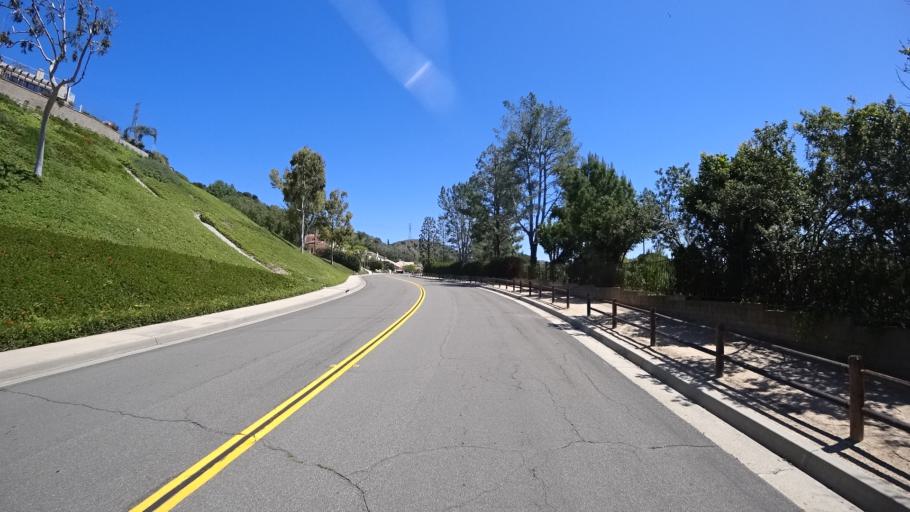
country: US
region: California
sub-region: Orange County
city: Villa Park
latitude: 33.8277
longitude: -117.8096
